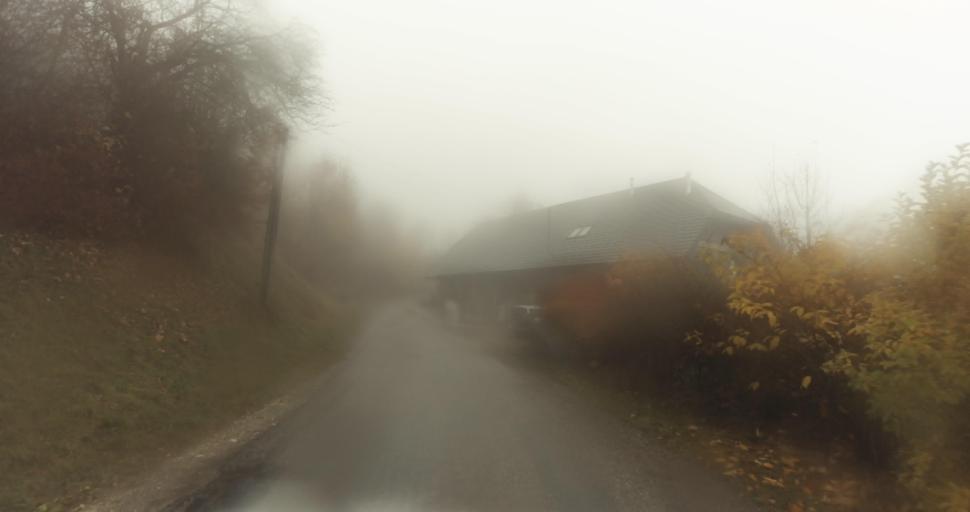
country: FR
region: Rhone-Alpes
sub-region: Departement de la Haute-Savoie
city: Villaz
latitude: 45.9752
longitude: 6.2131
